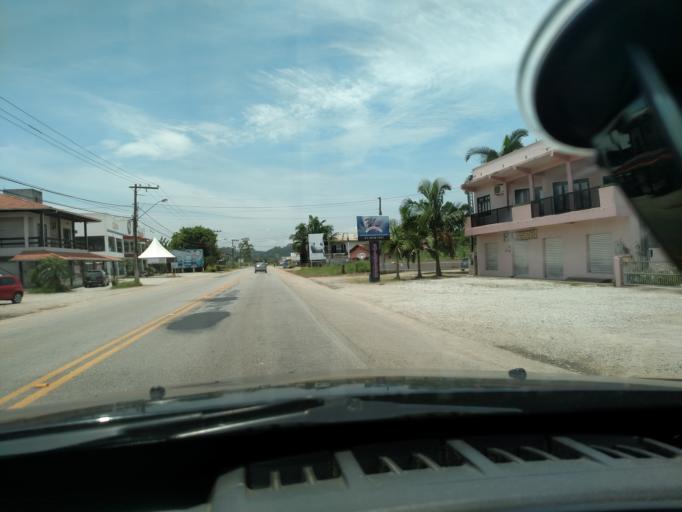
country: BR
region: Santa Catarina
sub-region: Gaspar
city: Gaspar
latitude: -26.9210
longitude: -48.9001
